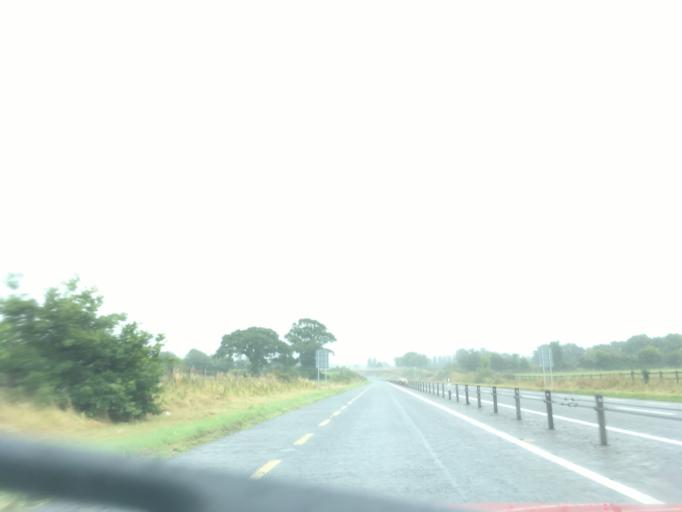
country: IE
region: Leinster
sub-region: Kilkenny
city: Piltown
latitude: 52.3503
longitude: -7.3382
